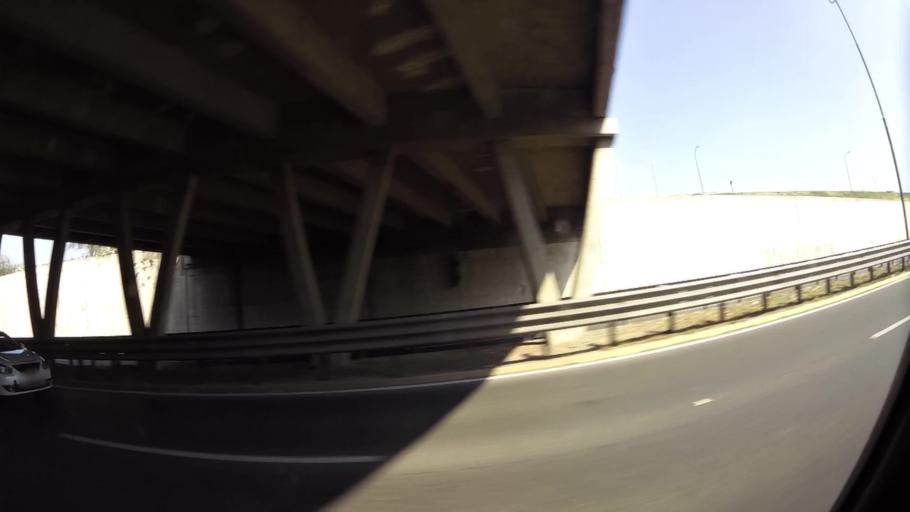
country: CL
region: Santiago Metropolitan
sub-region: Provincia de Santiago
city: Santiago
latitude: -33.4769
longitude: -70.6847
